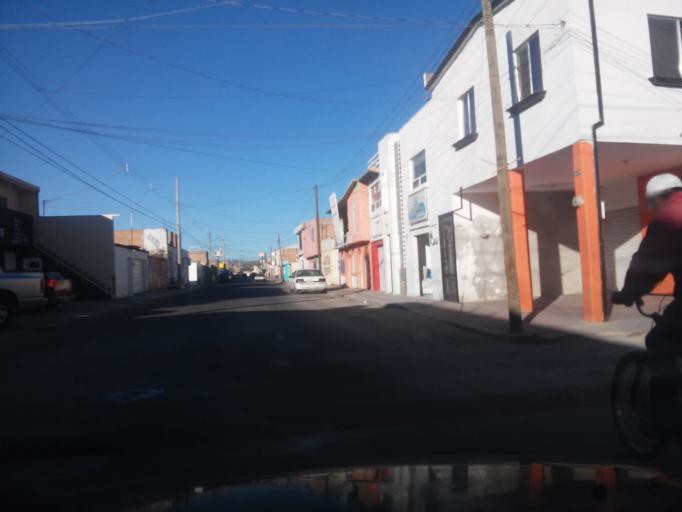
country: MX
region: Durango
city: Victoria de Durango
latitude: 24.0135
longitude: -104.6491
